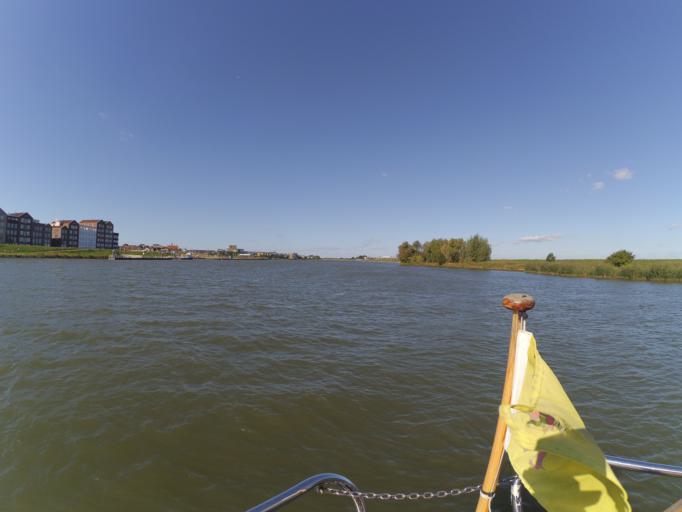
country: NL
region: South Holland
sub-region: Gemeente Oud-Beijerland
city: Oud-Beijerland
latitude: 51.8298
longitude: 4.4149
